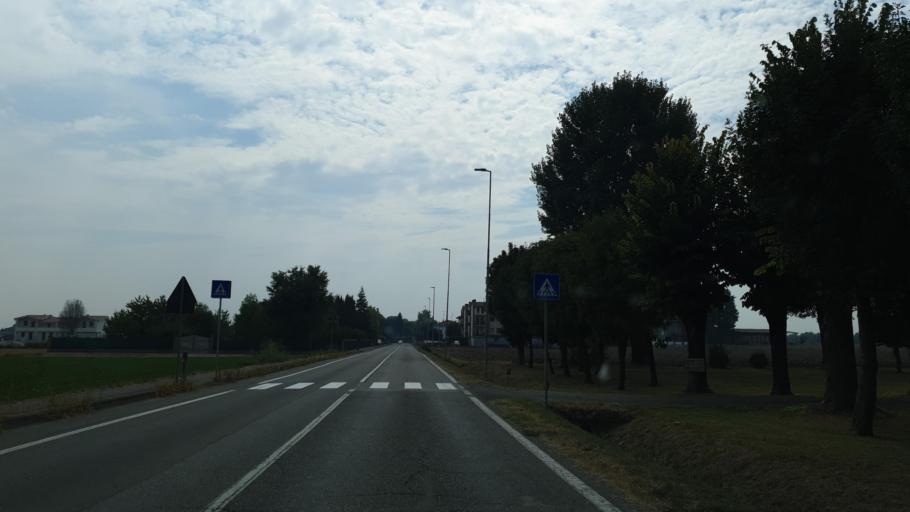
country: IT
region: Emilia-Romagna
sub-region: Provincia di Parma
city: San Secondo Parmense
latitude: 44.8755
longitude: 10.2512
